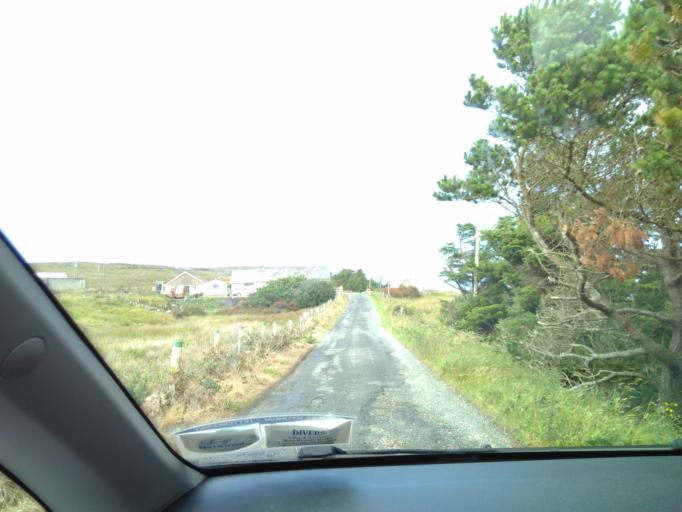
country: IE
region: Ulster
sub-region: County Donegal
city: Dungloe
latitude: 54.9916
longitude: -8.5076
